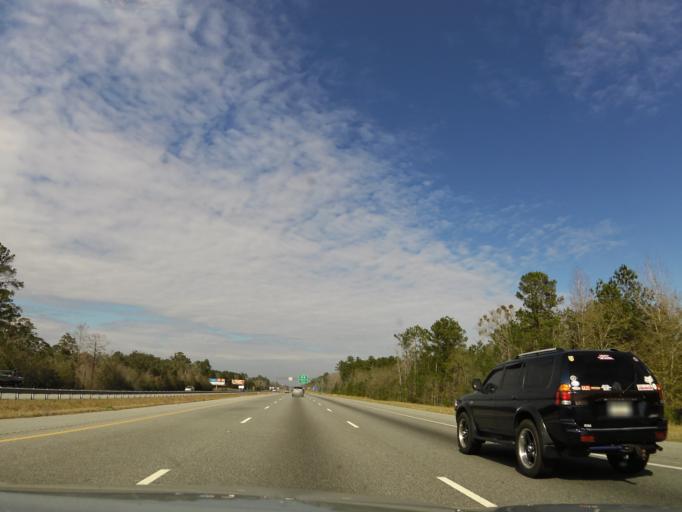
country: US
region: Georgia
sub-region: McIntosh County
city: Darien
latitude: 31.5101
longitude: -81.4460
